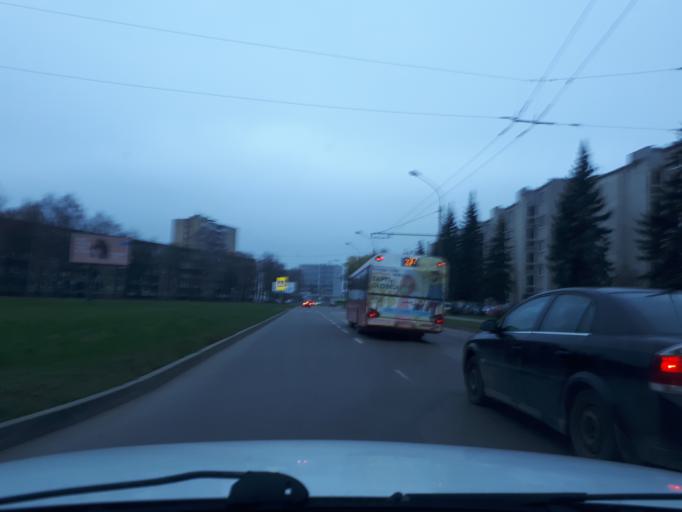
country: LT
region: Kauno apskritis
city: Dainava (Kaunas)
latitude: 54.9153
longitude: 23.9557
